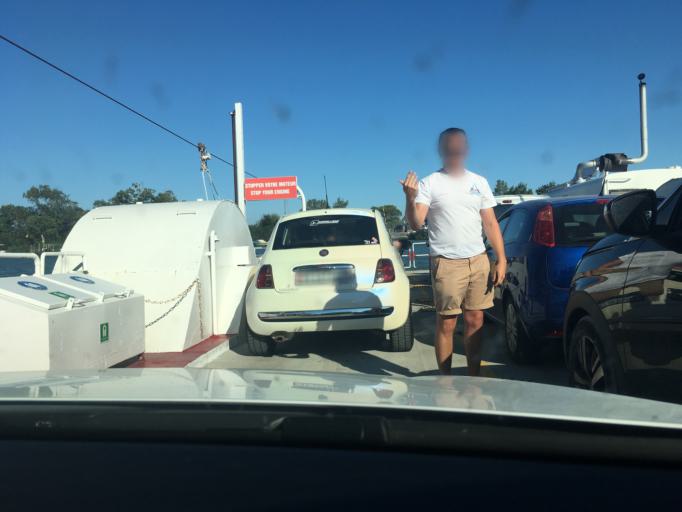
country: FR
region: Provence-Alpes-Cote d'Azur
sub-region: Departement des Bouches-du-Rhone
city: Saintes-Maries-de-la-Mer
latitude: 43.4870
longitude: 4.3831
